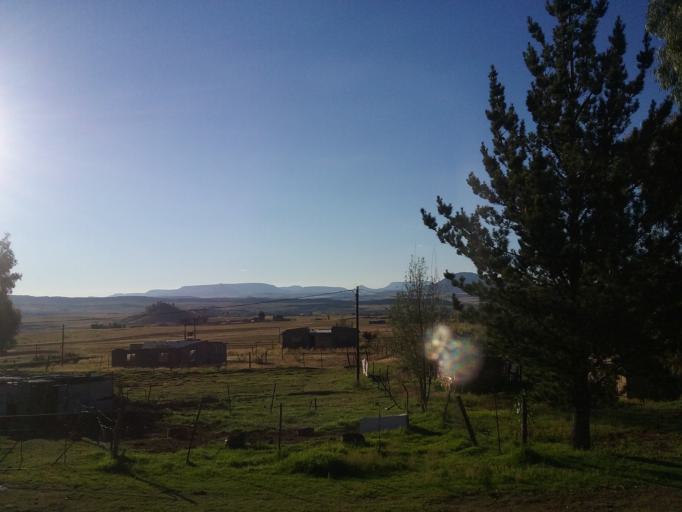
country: LS
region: Mohale's Hoek District
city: Mohale's Hoek
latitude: -30.1871
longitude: 27.4196
